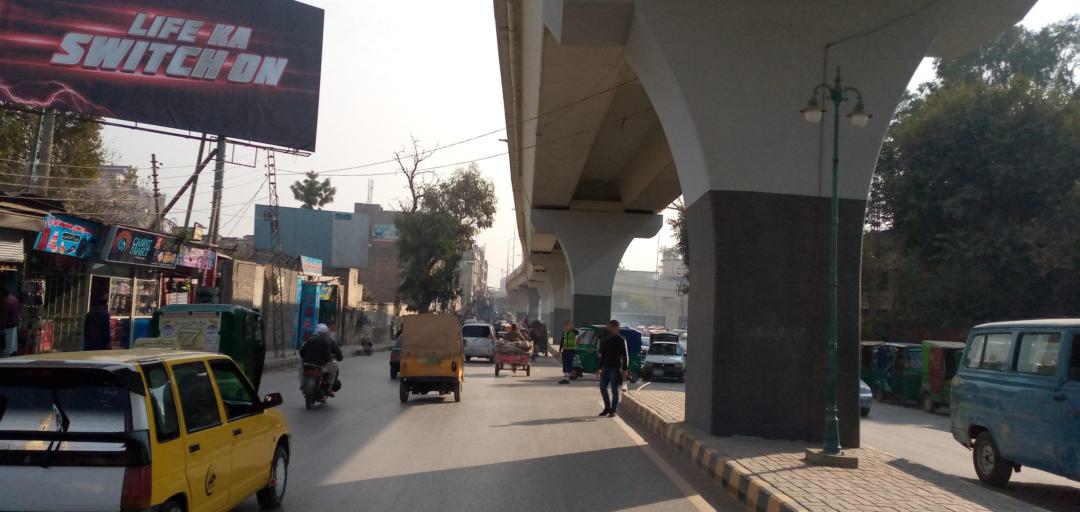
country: PK
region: Khyber Pakhtunkhwa
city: Peshawar
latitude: 33.9972
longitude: 71.5346
